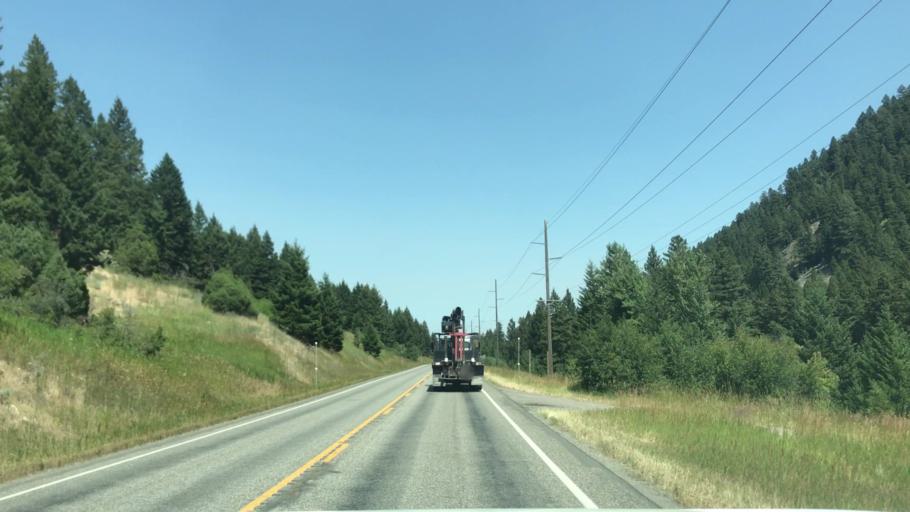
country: US
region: Montana
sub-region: Gallatin County
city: Four Corners
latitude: 45.5106
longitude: -111.2598
